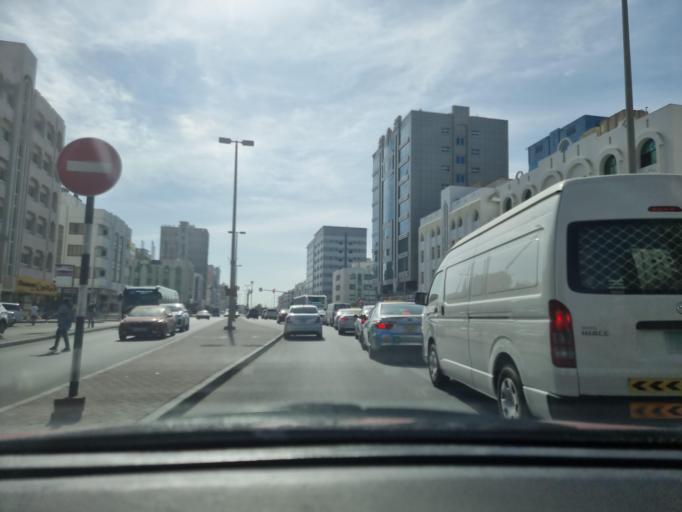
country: AE
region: Abu Dhabi
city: Abu Dhabi
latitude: 24.3258
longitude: 54.5352
